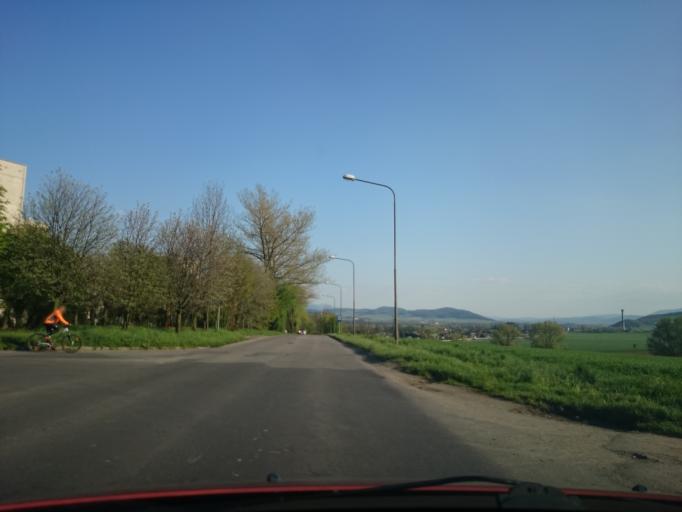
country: PL
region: Lower Silesian Voivodeship
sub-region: Powiat klodzki
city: Klodzko
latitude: 50.4343
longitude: 16.6385
